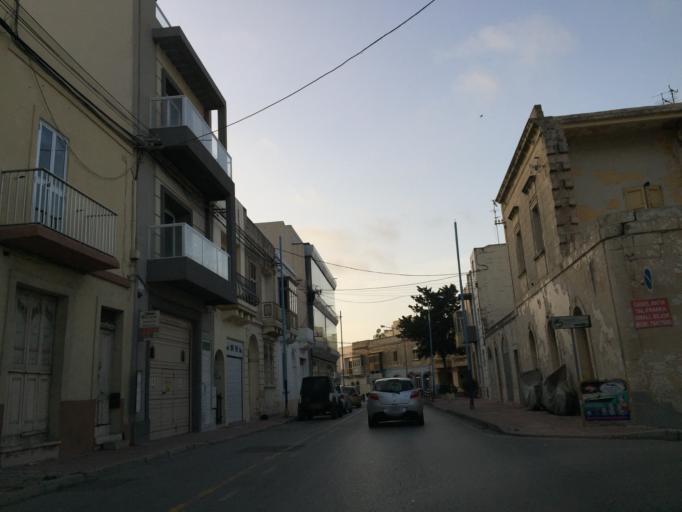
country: MT
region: Saint Paul's Bay
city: San Pawl il-Bahar
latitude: 35.9354
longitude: 14.4141
